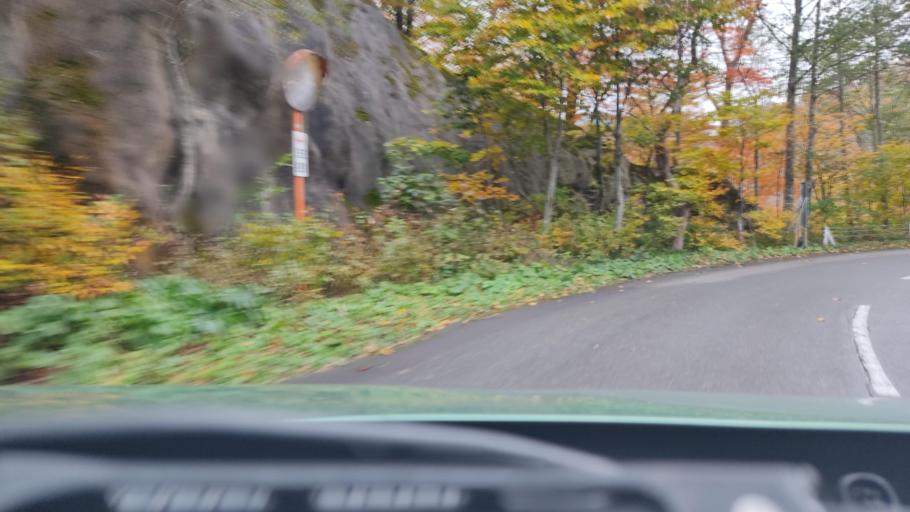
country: JP
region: Iwate
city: Mizusawa
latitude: 39.1256
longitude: 140.8270
